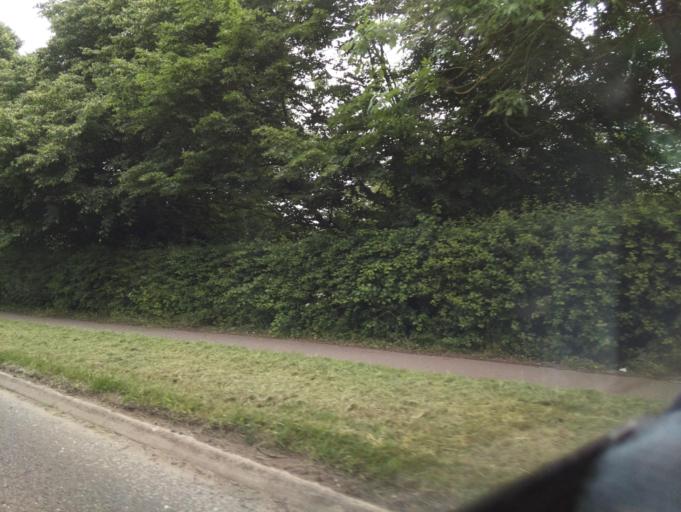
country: GB
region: England
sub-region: District of Rutland
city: Burley
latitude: 52.6684
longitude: -0.7066
